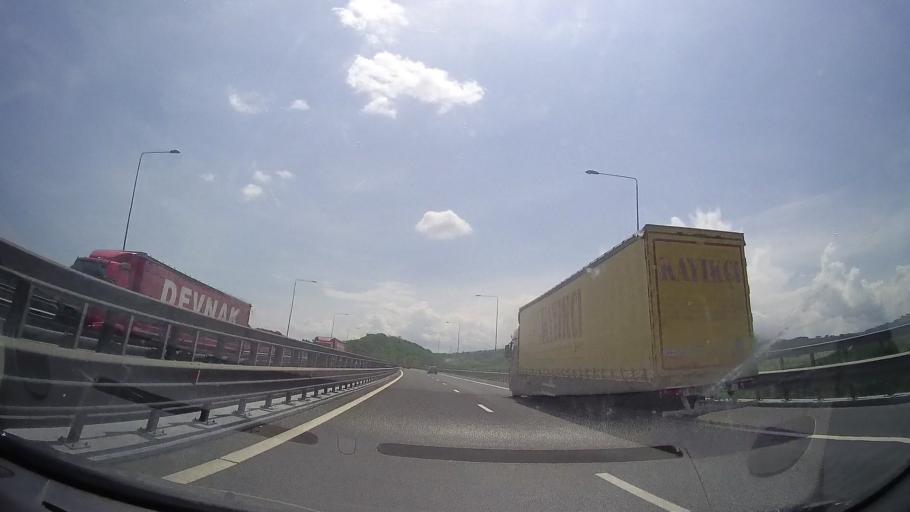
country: RO
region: Sibiu
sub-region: Comuna Tilisca
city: Tilisca
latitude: 45.8281
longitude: 23.8638
